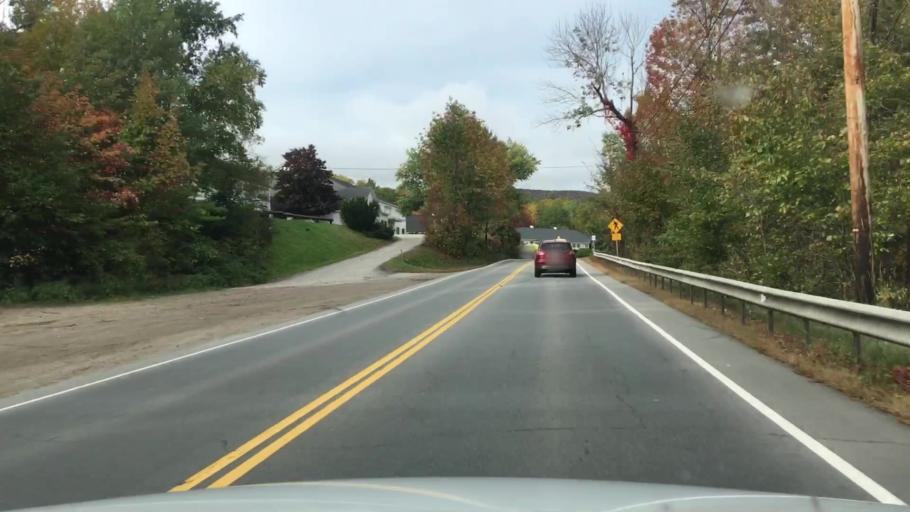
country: US
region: New Hampshire
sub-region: Coos County
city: Gorham
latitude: 44.3851
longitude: -71.1559
